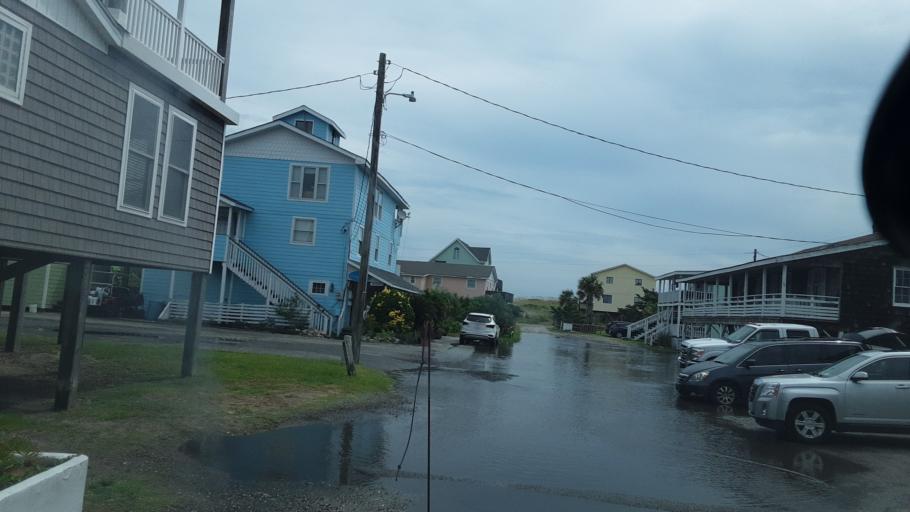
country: US
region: North Carolina
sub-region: Dare County
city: Buxton
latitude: 35.3526
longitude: -75.5022
